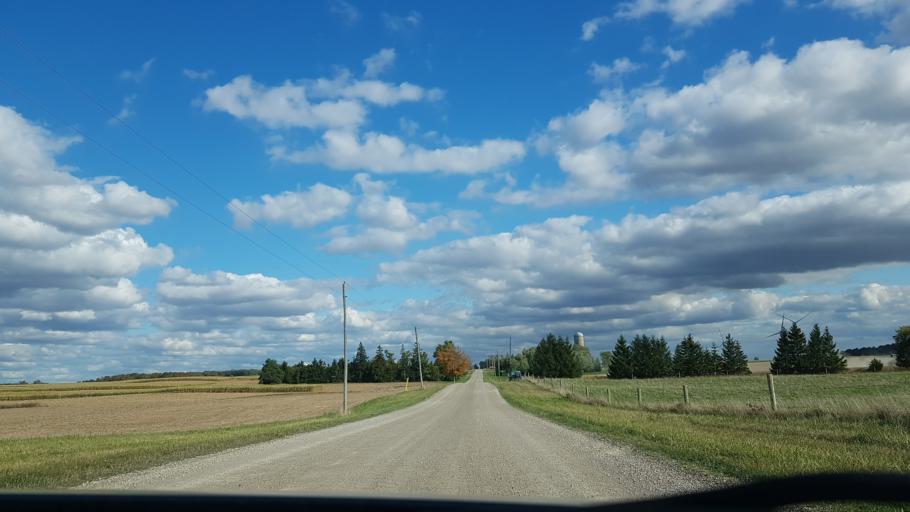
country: CA
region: Ontario
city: South Huron
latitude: 43.1150
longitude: -81.6620
